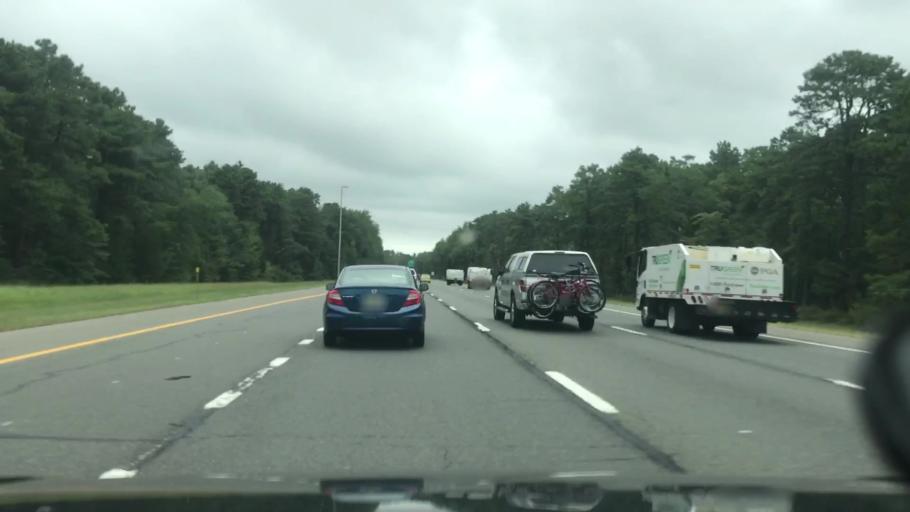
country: US
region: New Jersey
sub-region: Ocean County
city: Forked River
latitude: 39.8775
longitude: -74.2130
